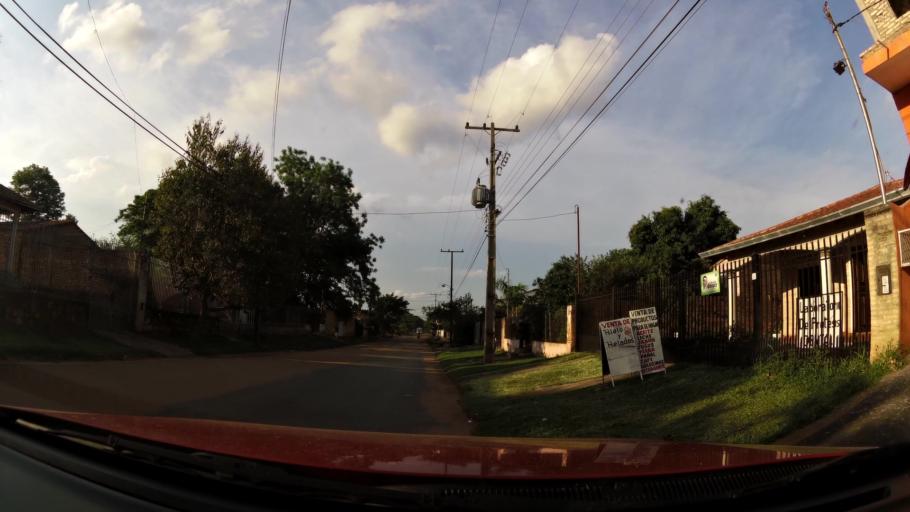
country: PY
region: Central
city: Fernando de la Mora
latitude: -25.3525
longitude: -57.5278
